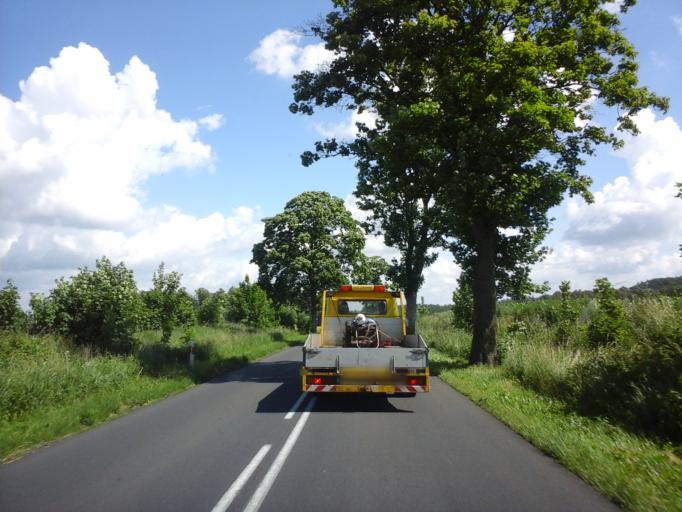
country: PL
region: West Pomeranian Voivodeship
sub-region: Powiat lobeski
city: Lobez
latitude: 53.6873
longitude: 15.6824
